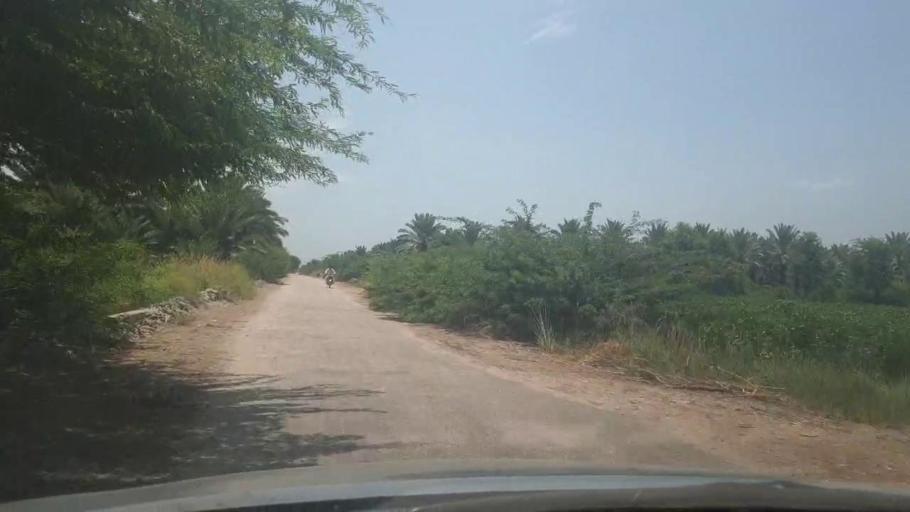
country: PK
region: Sindh
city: Kot Diji
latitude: 27.4030
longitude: 68.7234
